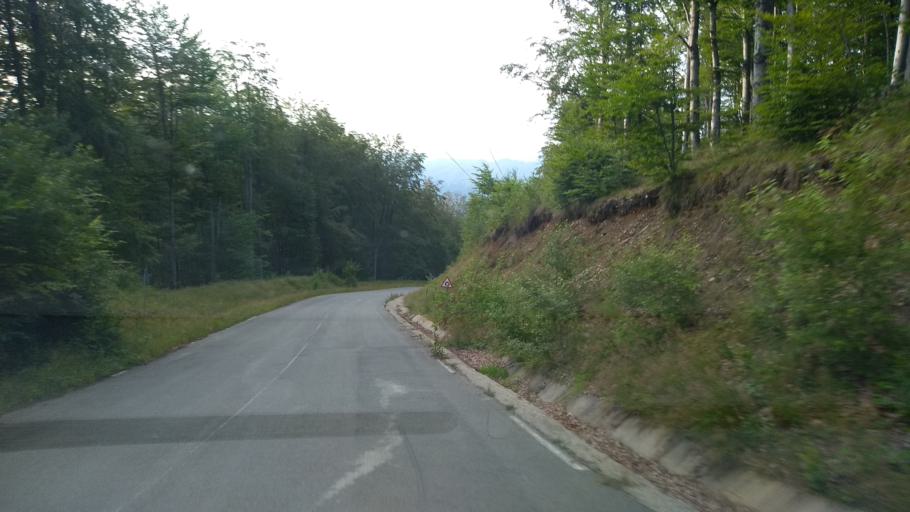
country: RO
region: Hunedoara
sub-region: Municipiul  Vulcan
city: Jiu-Paroseni
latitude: 45.3383
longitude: 23.2912
